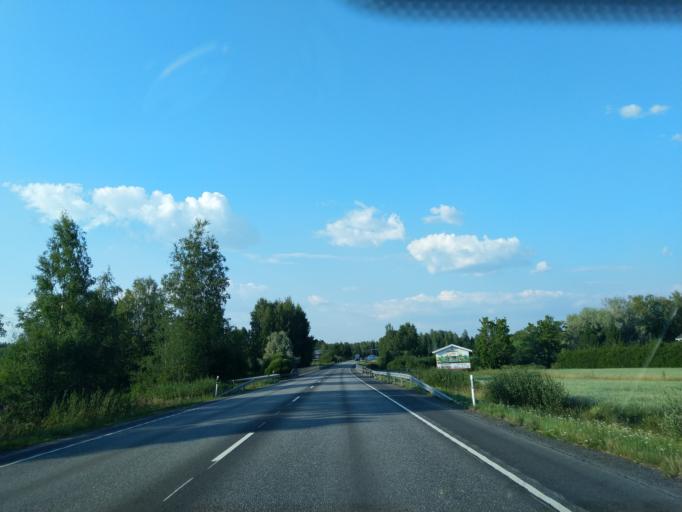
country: FI
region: Satakunta
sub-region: Pori
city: Pomarkku
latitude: 61.6952
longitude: 22.0046
